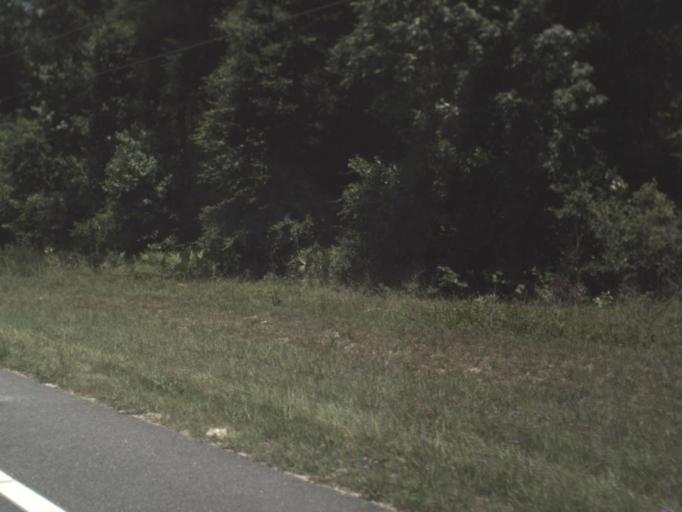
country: US
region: Florida
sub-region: Levy County
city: Manatee Road
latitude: 29.6255
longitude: -82.9832
